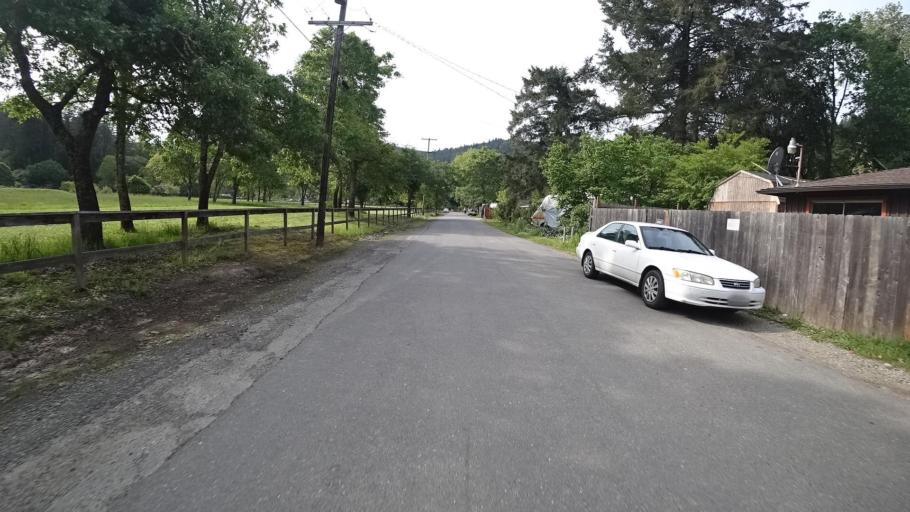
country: US
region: California
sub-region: Humboldt County
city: Redway
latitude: 40.2102
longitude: -123.7898
